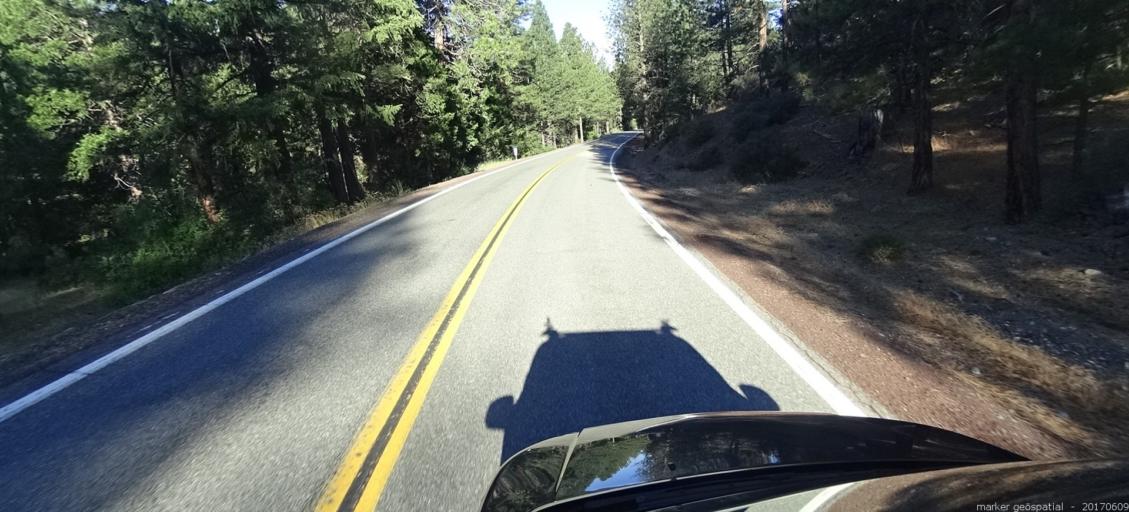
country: US
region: California
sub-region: Siskiyou County
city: Weed
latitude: 41.4022
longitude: -122.6406
